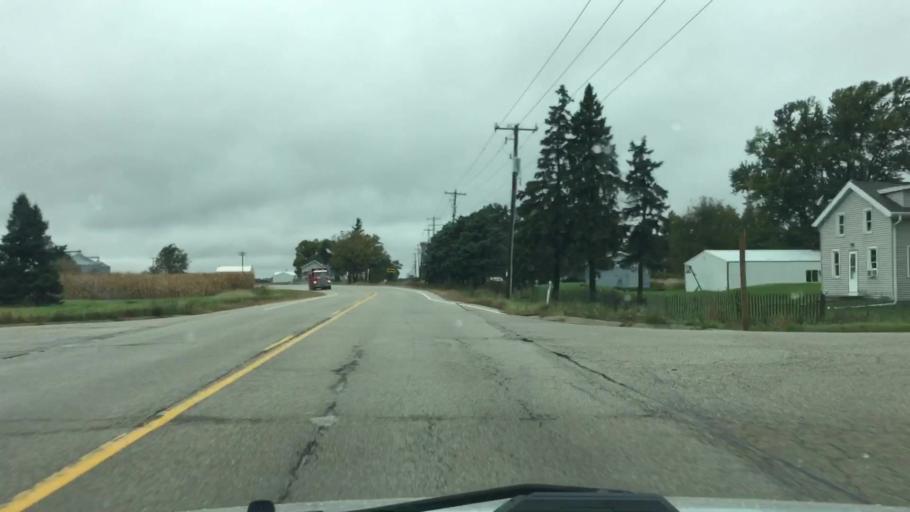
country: US
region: Wisconsin
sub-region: Walworth County
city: Whitewater
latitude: 42.8056
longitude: -88.7831
